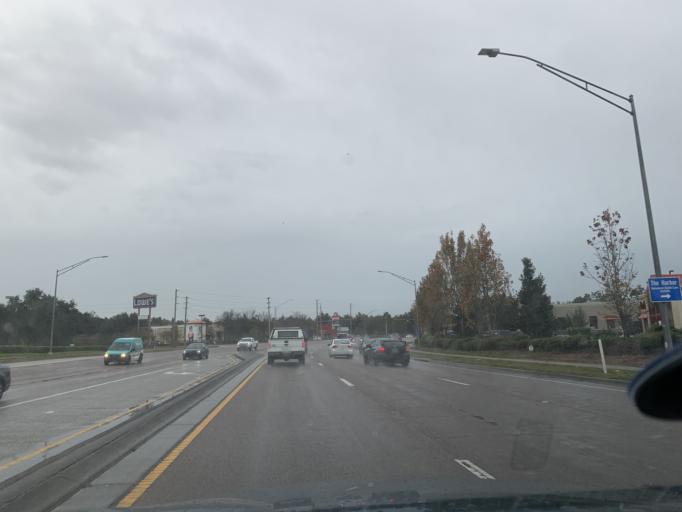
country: US
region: Florida
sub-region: Pasco County
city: Jasmine Estates
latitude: 28.2784
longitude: -82.6752
